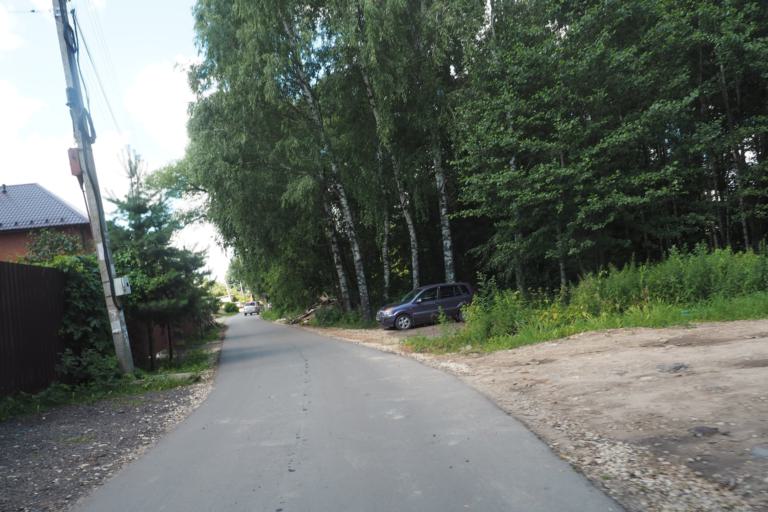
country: RU
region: Moskovskaya
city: Ramenskoye
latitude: 55.5793
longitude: 38.2661
